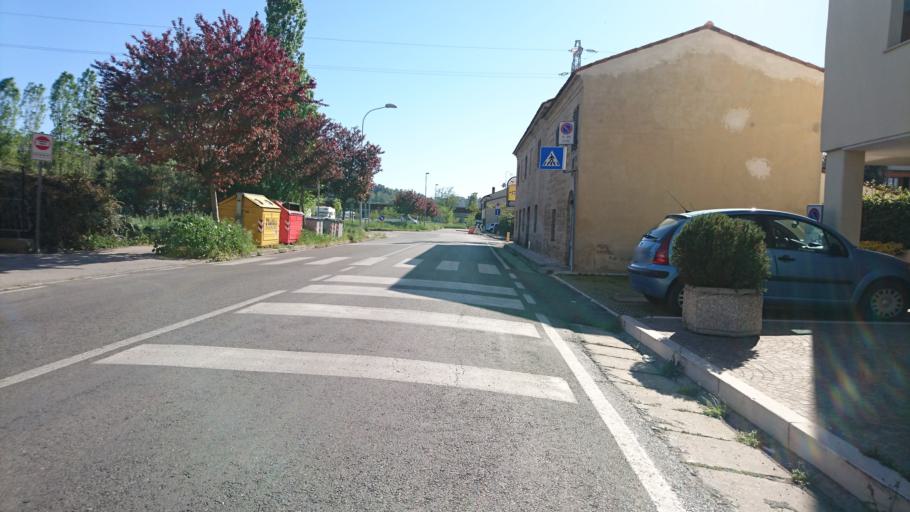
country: IT
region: The Marches
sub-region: Provincia di Pesaro e Urbino
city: Pesaro
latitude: 43.8931
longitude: 12.8879
